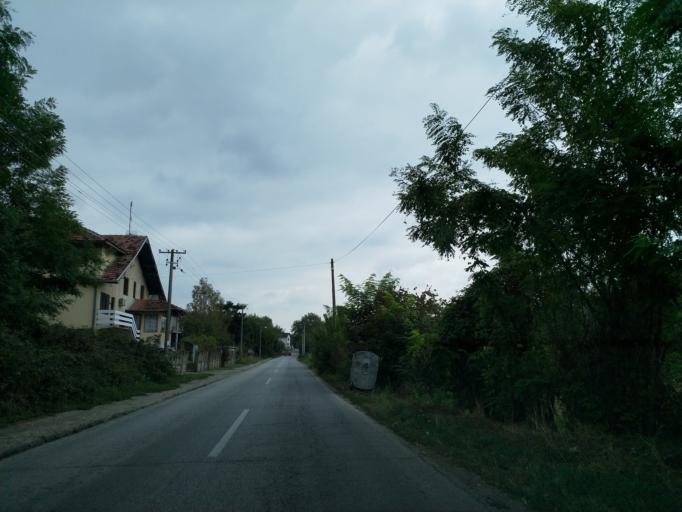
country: RS
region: Central Serbia
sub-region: Pomoravski Okrug
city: Jagodina
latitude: 44.0706
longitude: 21.1789
